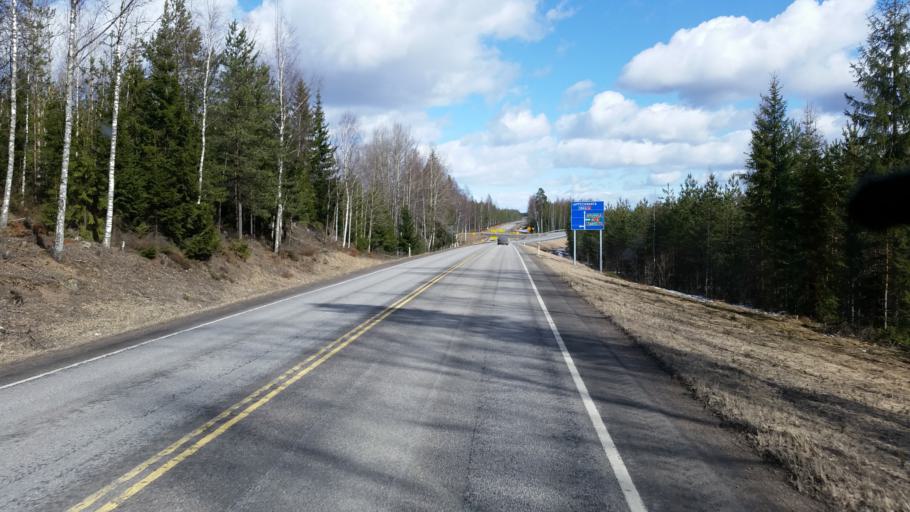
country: FI
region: South Karelia
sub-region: Lappeenranta
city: Lemi
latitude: 60.9749
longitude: 27.8630
